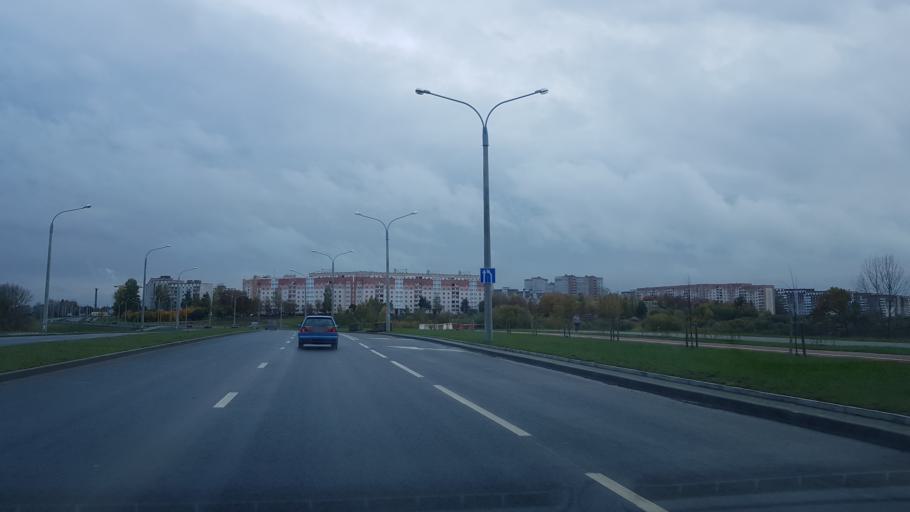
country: BY
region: Minsk
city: Syenitsa
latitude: 53.8585
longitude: 27.5574
